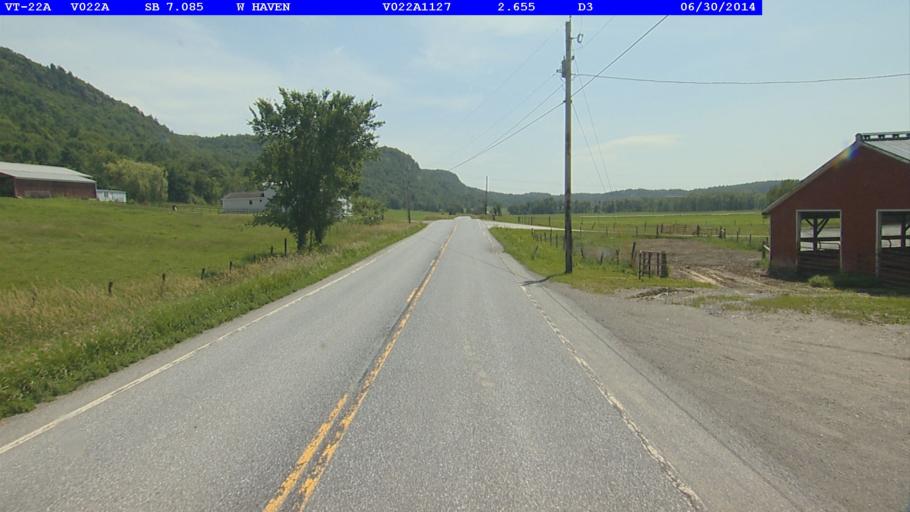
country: US
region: Vermont
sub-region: Rutland County
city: Fair Haven
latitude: 43.6644
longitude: -73.2906
